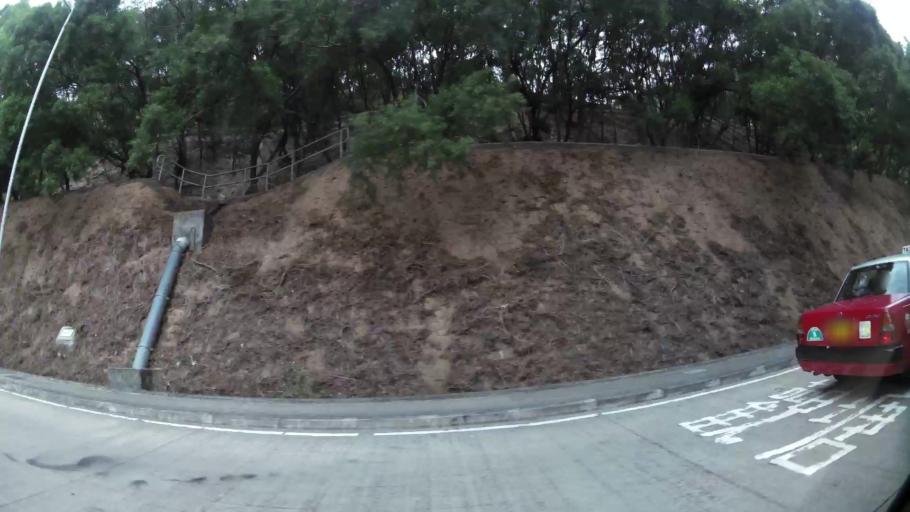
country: HK
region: Sham Shui Po
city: Sham Shui Po
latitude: 22.3427
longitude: 114.1595
